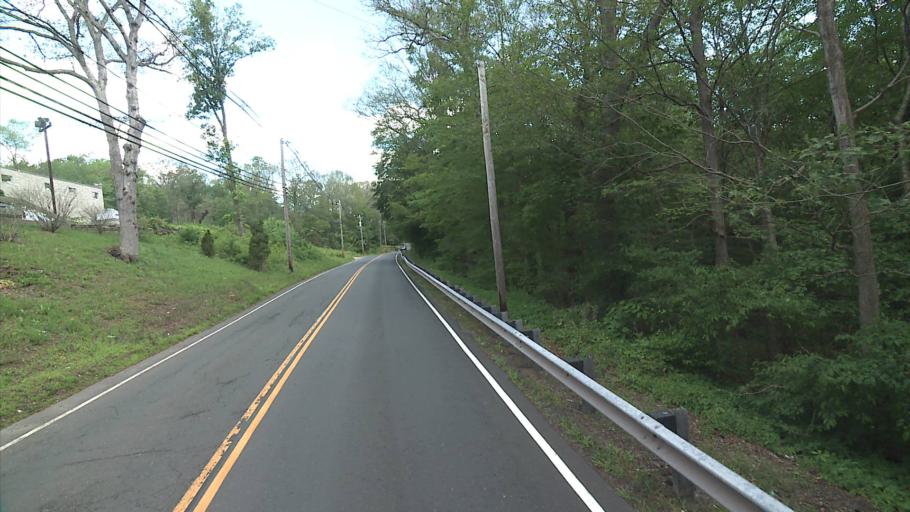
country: US
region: Connecticut
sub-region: Middlesex County
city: East Hampton
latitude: 41.5675
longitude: -72.5061
